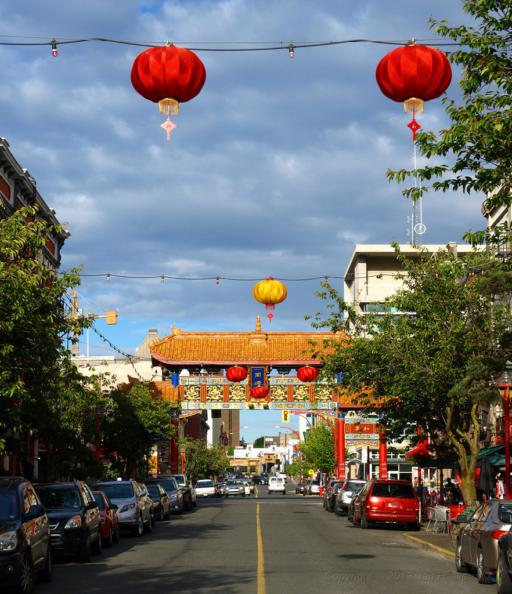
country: CA
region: British Columbia
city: Victoria
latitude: 48.4294
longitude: -123.3680
